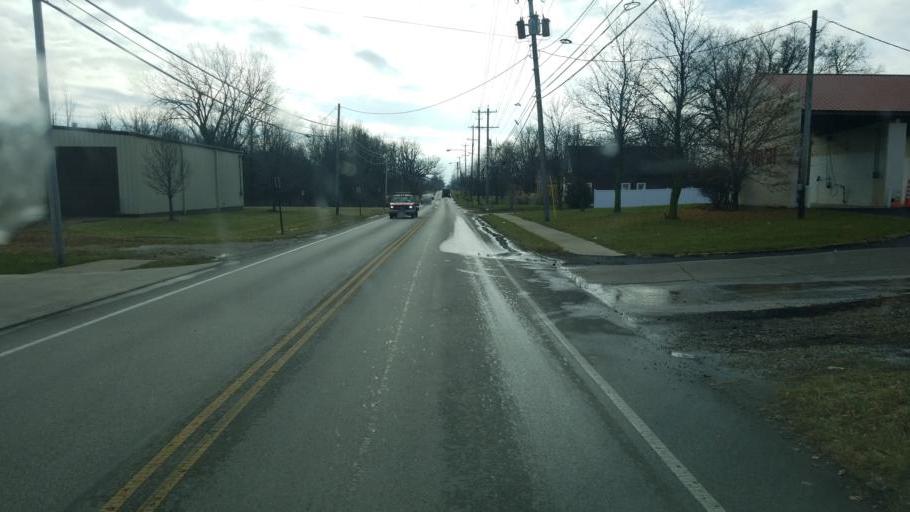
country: US
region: Ohio
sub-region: Delaware County
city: Delaware
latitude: 40.2898
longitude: -83.0797
